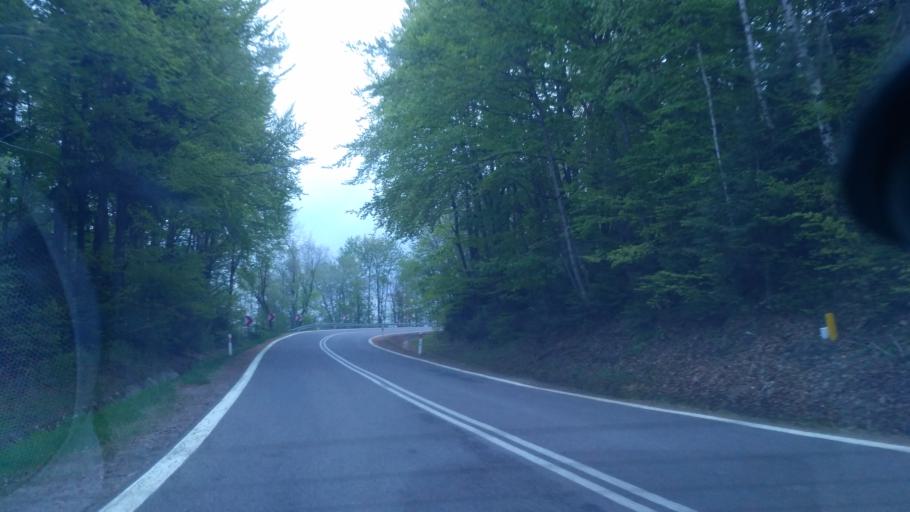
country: PL
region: Subcarpathian Voivodeship
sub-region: Powiat sanocki
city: Tyrawa Woloska
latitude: 49.5648
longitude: 22.3403
